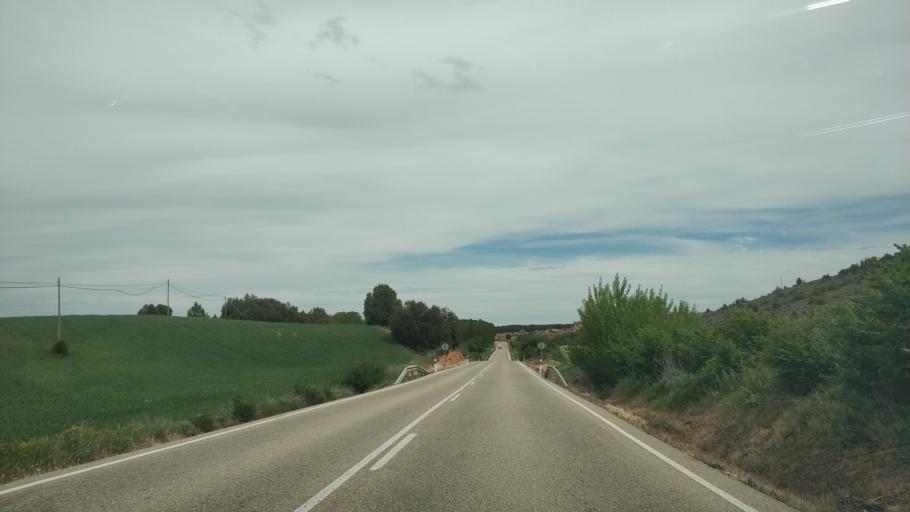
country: ES
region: Castille and Leon
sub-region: Provincia de Soria
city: El Burgo de Osma
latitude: 41.5741
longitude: -3.0189
